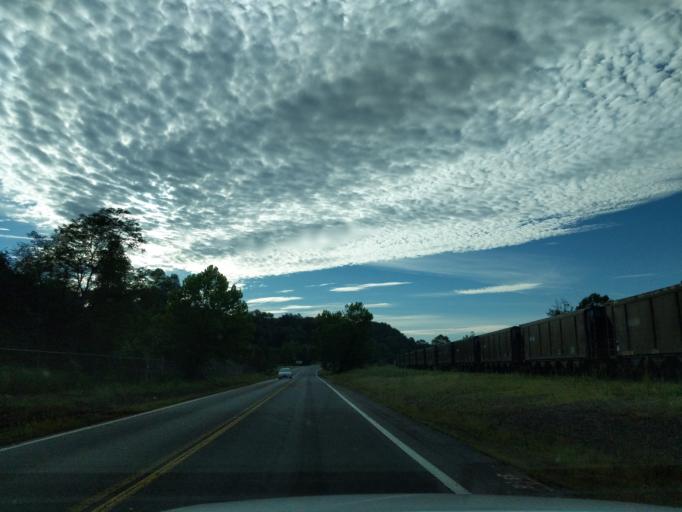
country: US
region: Georgia
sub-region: Fannin County
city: McCaysville
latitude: 34.9932
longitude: -84.3794
